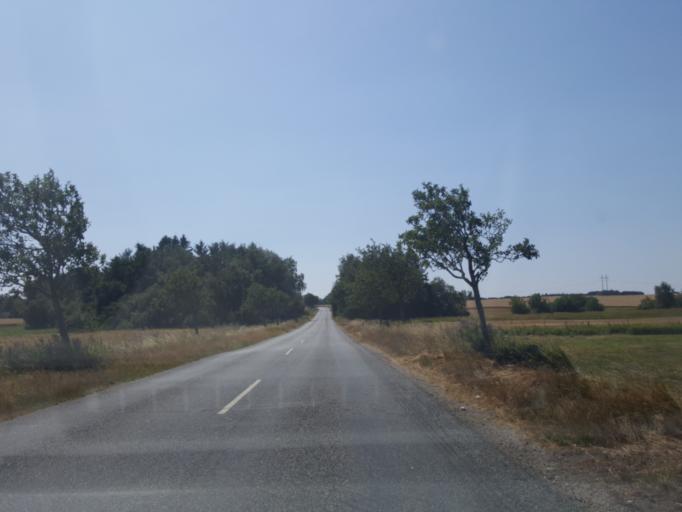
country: DK
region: Capital Region
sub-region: Fredensborg Kommune
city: Niva
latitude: 55.9344
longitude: 12.4737
